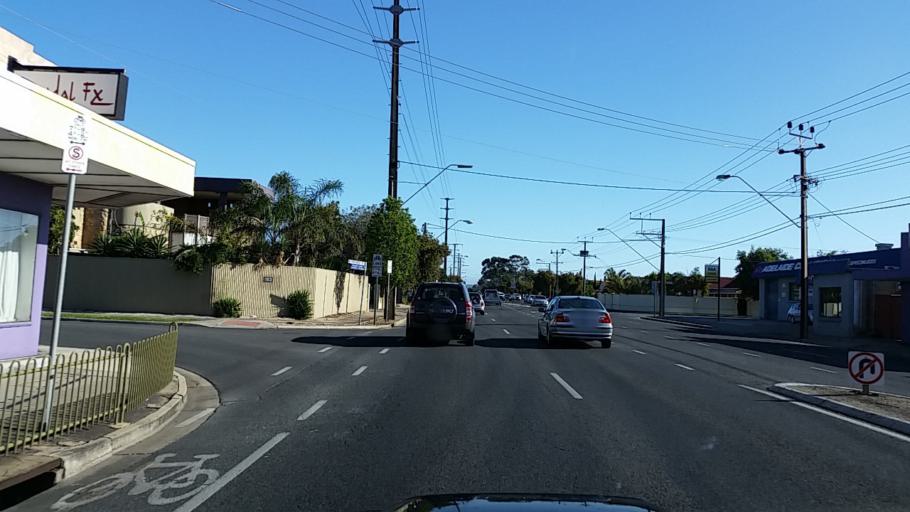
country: AU
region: South Australia
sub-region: City of West Torrens
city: Plympton
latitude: -34.9391
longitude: 138.5530
